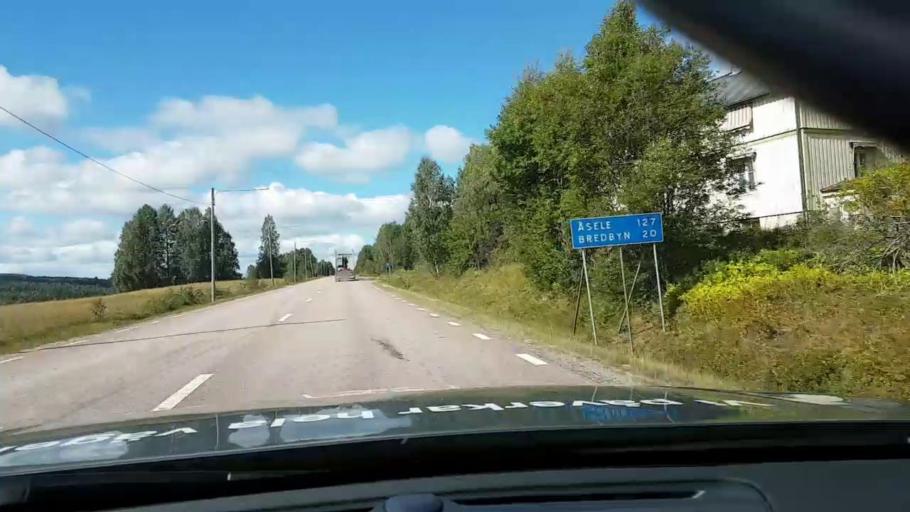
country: SE
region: Vaesternorrland
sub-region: OErnskoeldsviks Kommun
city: Bjasta
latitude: 63.3820
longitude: 18.4070
